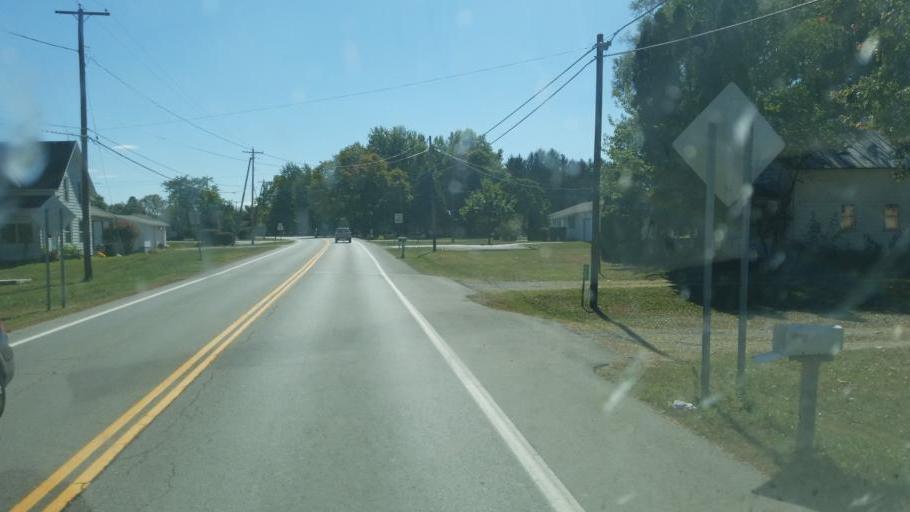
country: US
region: Ohio
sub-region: Huron County
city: Plymouth
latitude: 41.0295
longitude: -82.6812
